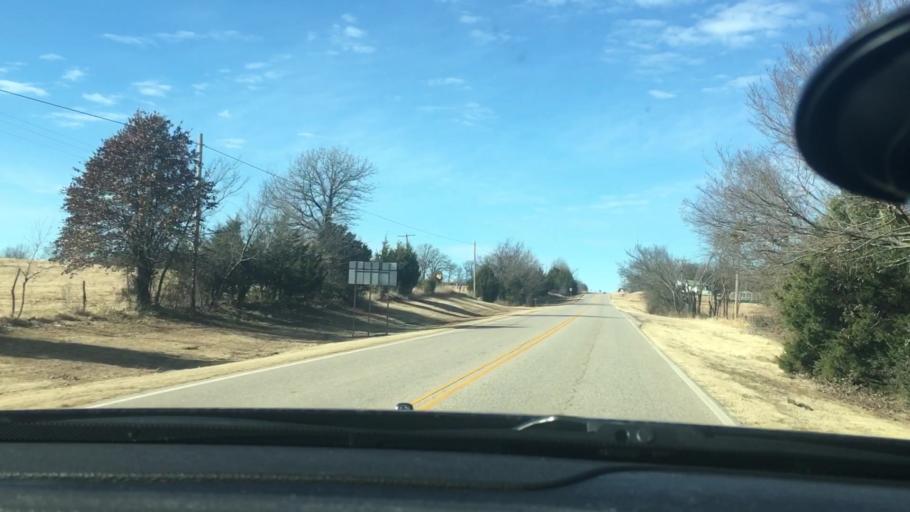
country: US
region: Oklahoma
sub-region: Seminole County
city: Konawa
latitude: 34.9860
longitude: -96.9362
